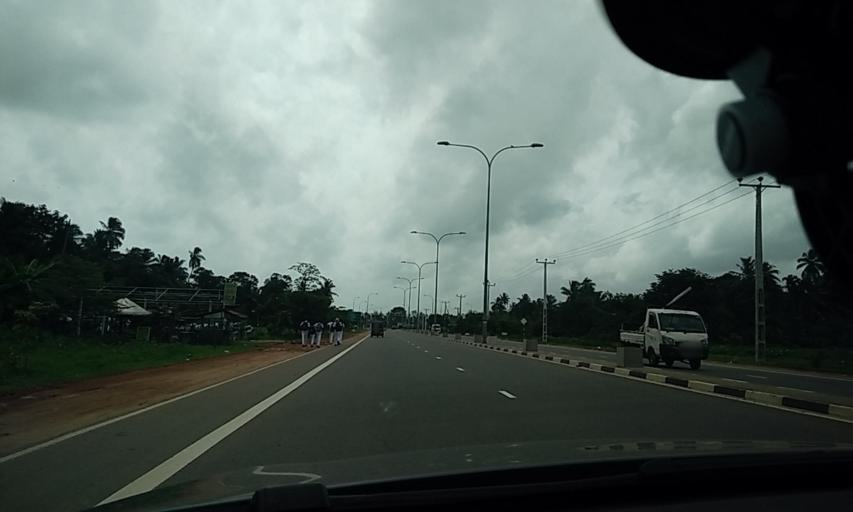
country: LK
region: Western
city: Maharagama
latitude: 6.8038
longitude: 79.9283
